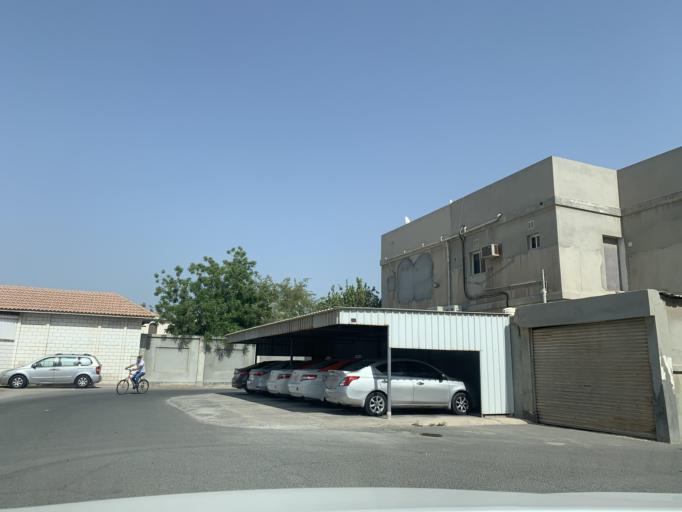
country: BH
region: Manama
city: Jidd Hafs
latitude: 26.2309
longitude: 50.4765
